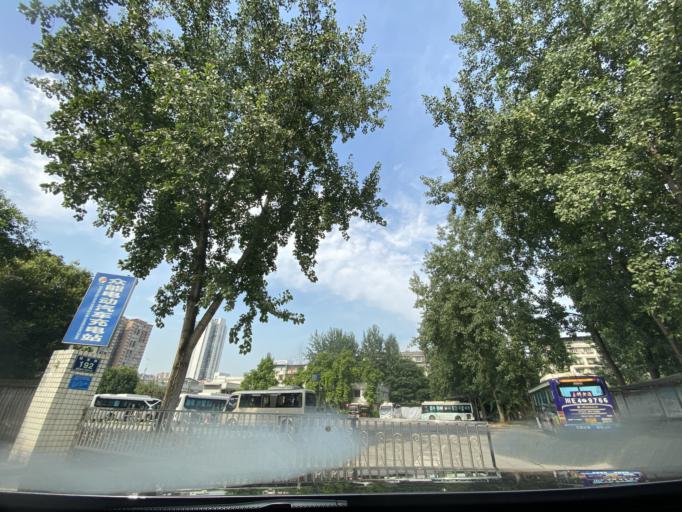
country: CN
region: Sichuan
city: Fuji
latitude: 29.1553
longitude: 105.3654
